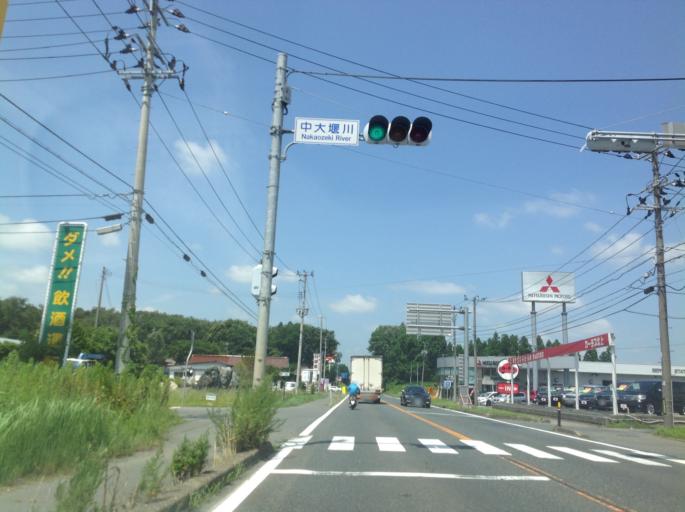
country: JP
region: Iwate
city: Hanamaki
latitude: 39.3389
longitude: 141.1083
